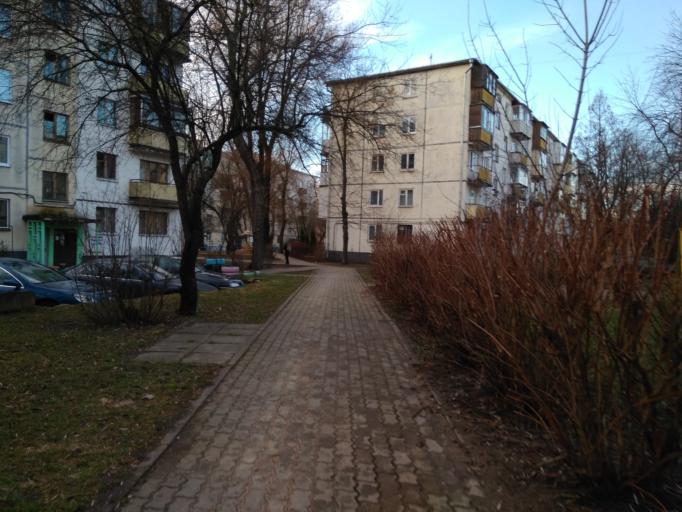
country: BY
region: Minsk
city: Minsk
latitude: 53.9002
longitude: 27.6051
